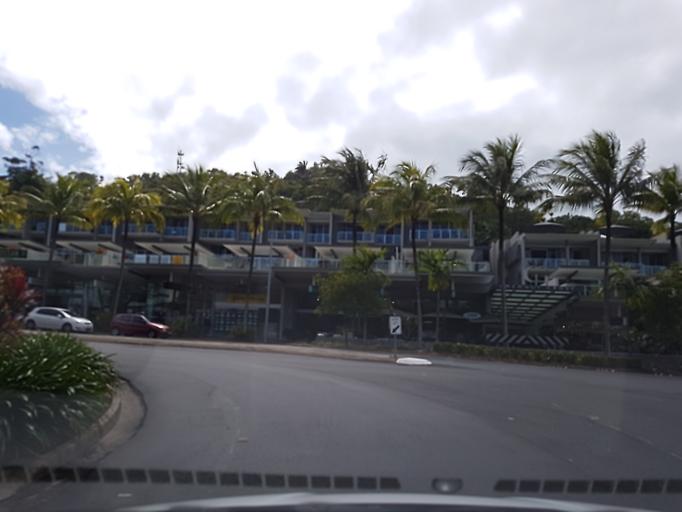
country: AU
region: Queensland
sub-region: Cairns
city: Port Douglas
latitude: -16.4849
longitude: 145.4666
